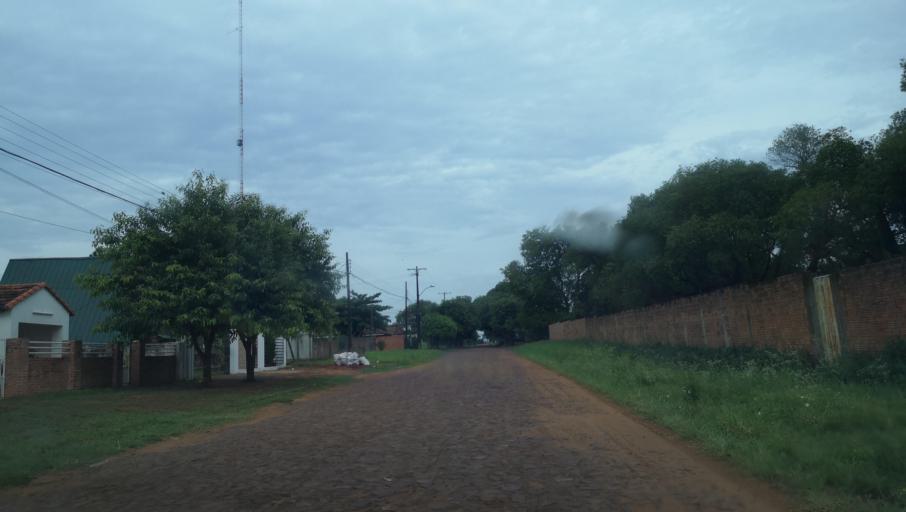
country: PY
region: Misiones
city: Santa Maria
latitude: -26.8805
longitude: -57.0281
